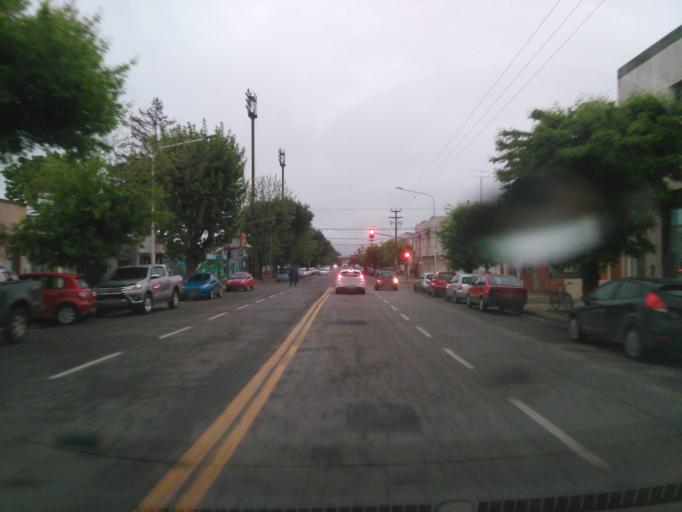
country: AR
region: Buenos Aires
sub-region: Partido de Tandil
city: Tandil
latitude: -37.3337
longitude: -59.1425
